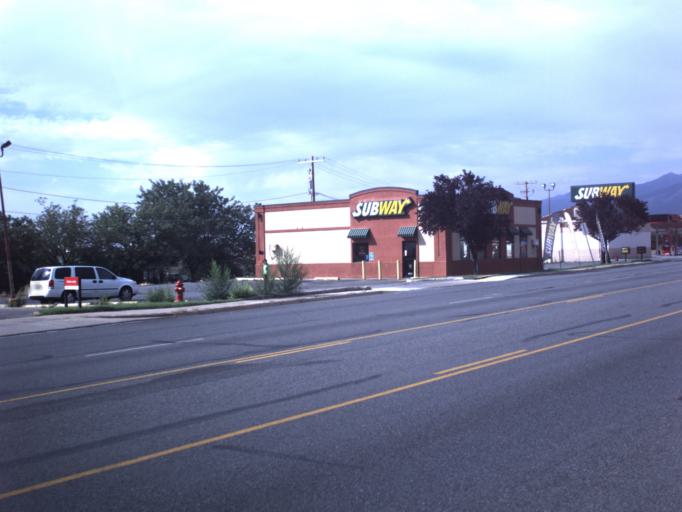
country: US
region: Utah
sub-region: Davis County
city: Woods Cross
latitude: 40.8603
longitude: -111.8973
